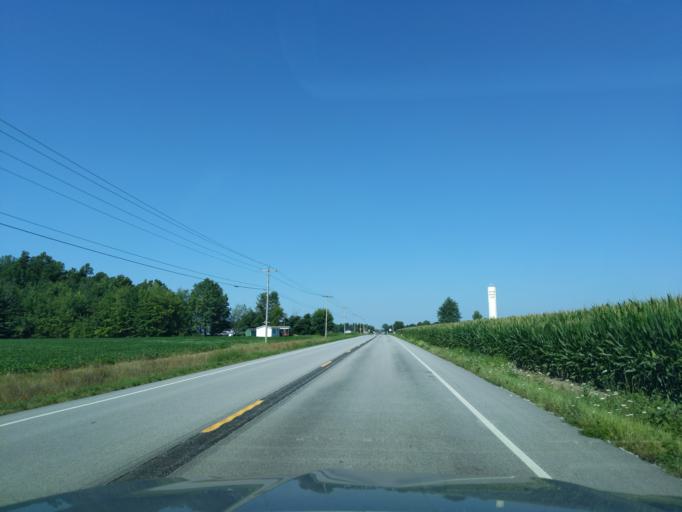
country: US
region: Indiana
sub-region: Ripley County
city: Osgood
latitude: 39.0752
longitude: -85.3441
